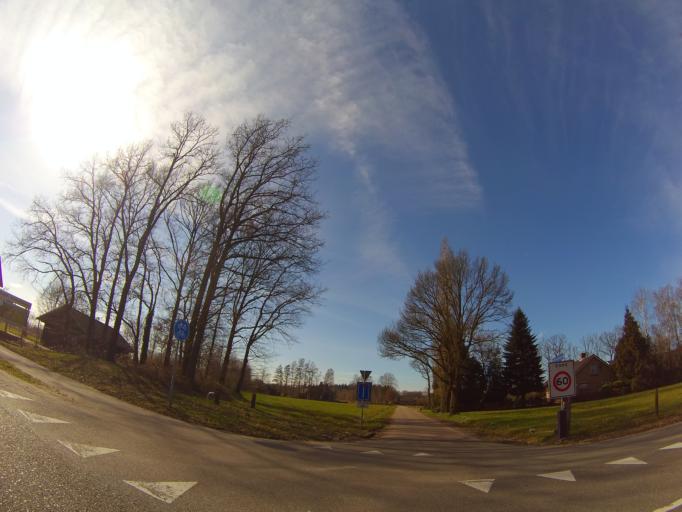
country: NL
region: Gelderland
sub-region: Gemeente Ede
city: Ederveen
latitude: 52.0829
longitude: 5.5393
